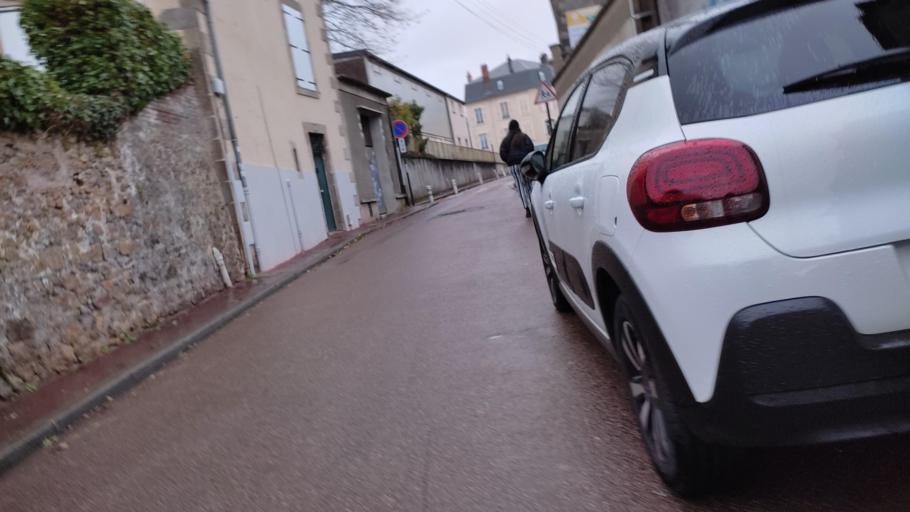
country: FR
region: Limousin
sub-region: Departement de la Haute-Vienne
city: Limoges
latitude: 45.8285
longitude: 1.2518
